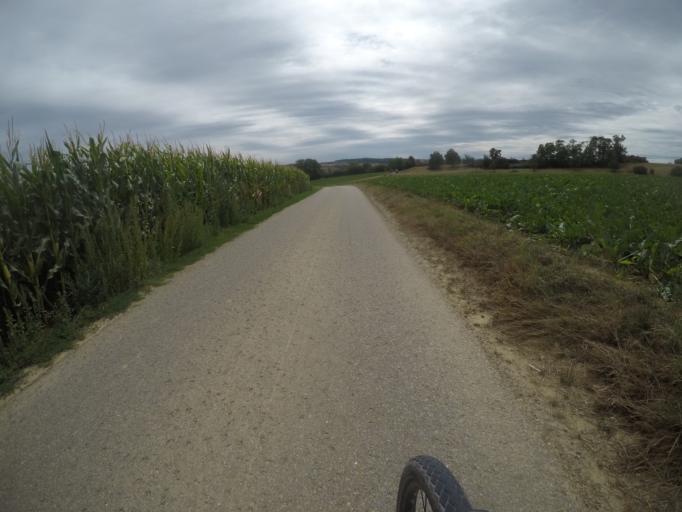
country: DE
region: Baden-Wuerttemberg
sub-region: Regierungsbezirk Stuttgart
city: Oberriexingen
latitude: 48.9310
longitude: 8.9944
